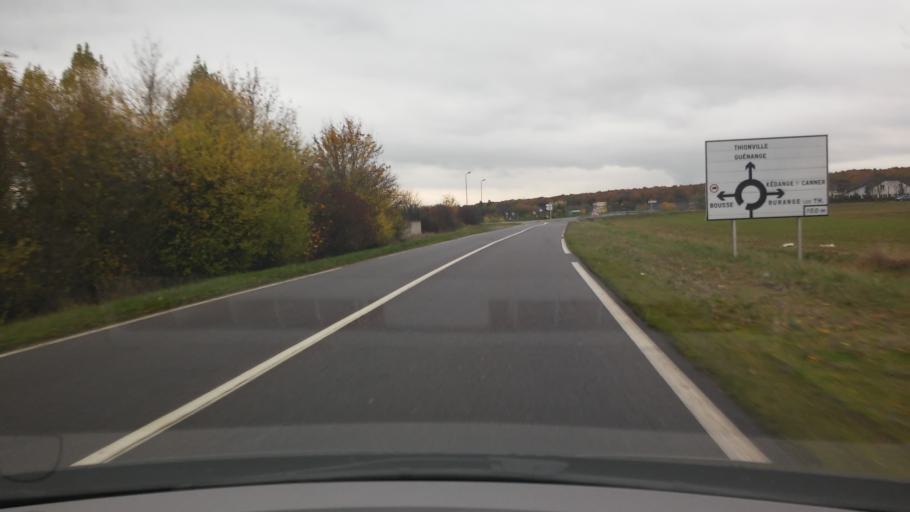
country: FR
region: Lorraine
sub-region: Departement de la Moselle
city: Bousse
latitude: 49.2732
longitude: 6.2015
